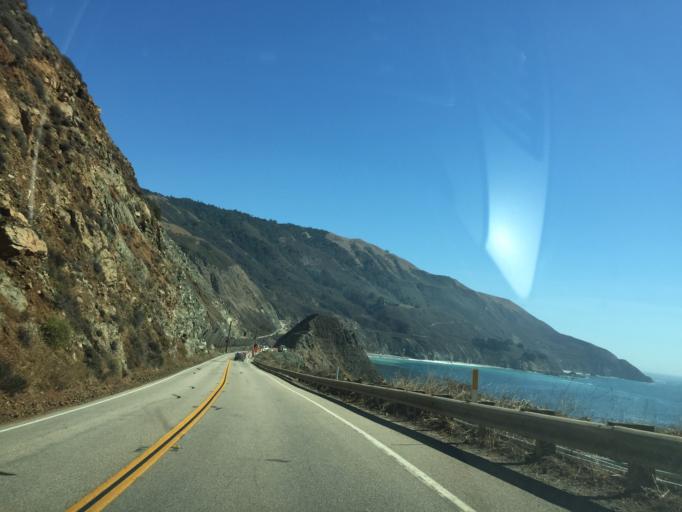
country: US
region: California
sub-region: Monterey County
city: Greenfield
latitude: 36.0722
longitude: -121.6053
